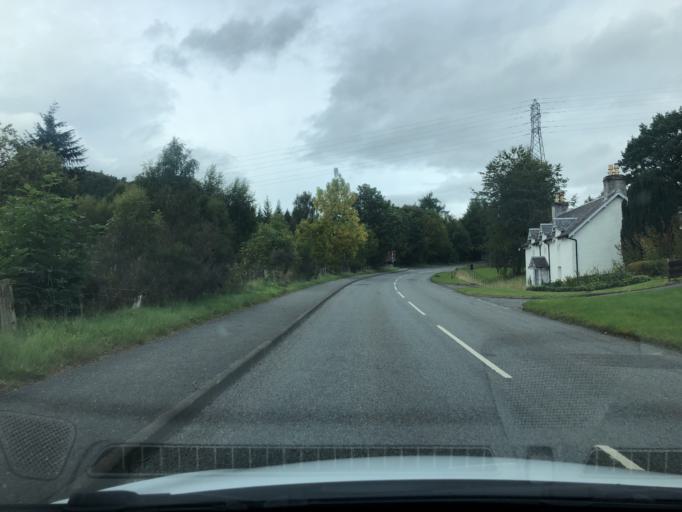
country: GB
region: Scotland
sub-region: Perth and Kinross
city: Pitlochry
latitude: 56.7251
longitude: -3.7746
